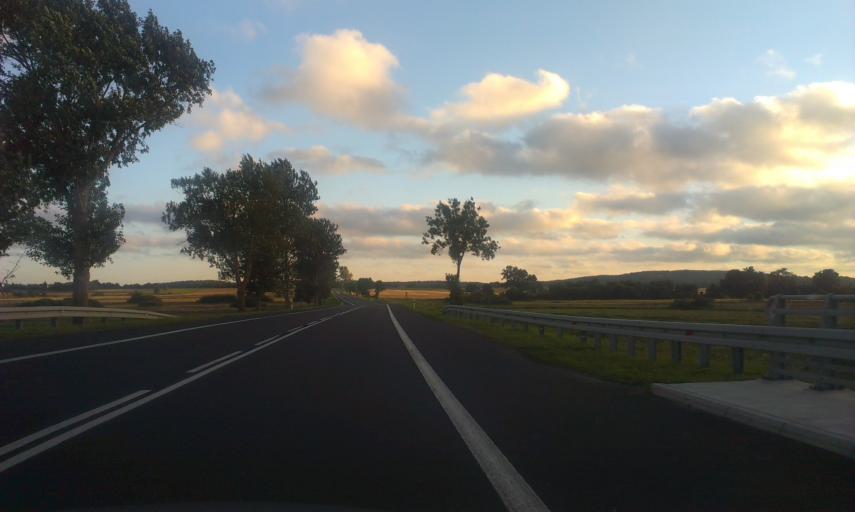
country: PL
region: West Pomeranian Voivodeship
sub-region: Powiat slawienski
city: Darlowo
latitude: 54.2910
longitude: 16.4936
